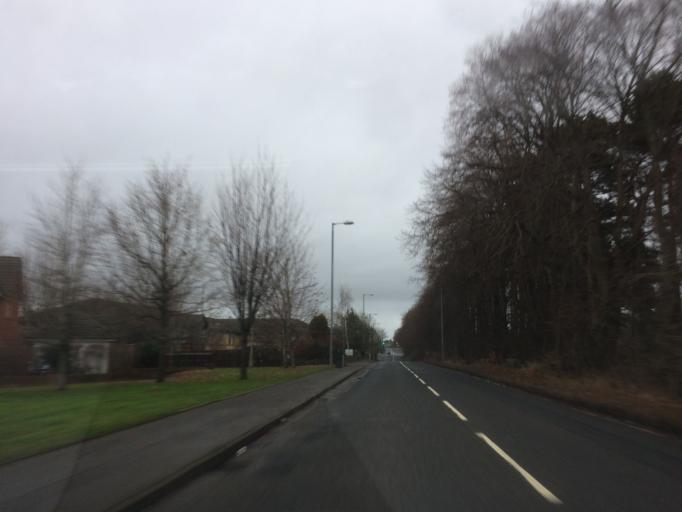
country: GB
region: Scotland
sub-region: East Renfrewshire
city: Newton Mearns
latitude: 55.7962
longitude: -4.3288
